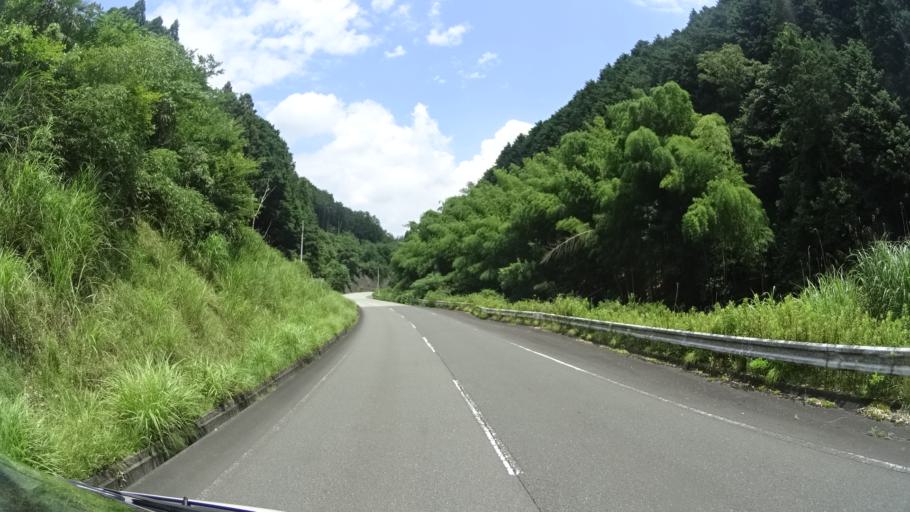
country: JP
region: Hyogo
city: Sasayama
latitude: 35.1772
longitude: 135.2434
